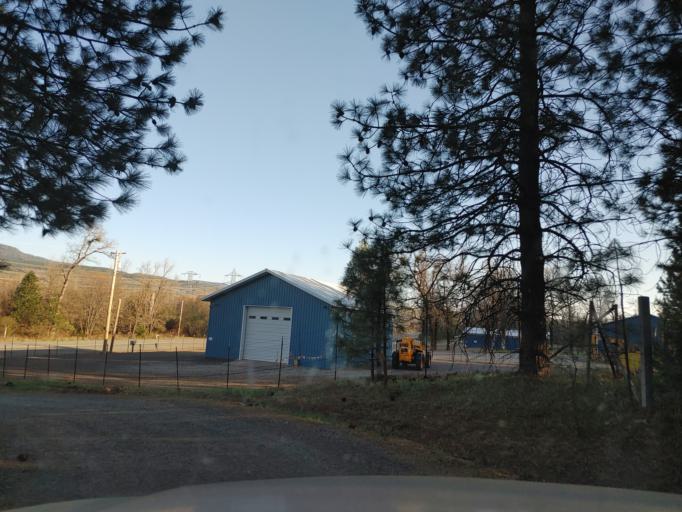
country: US
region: California
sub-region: Shasta County
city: Burney
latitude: 40.8083
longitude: -121.9407
